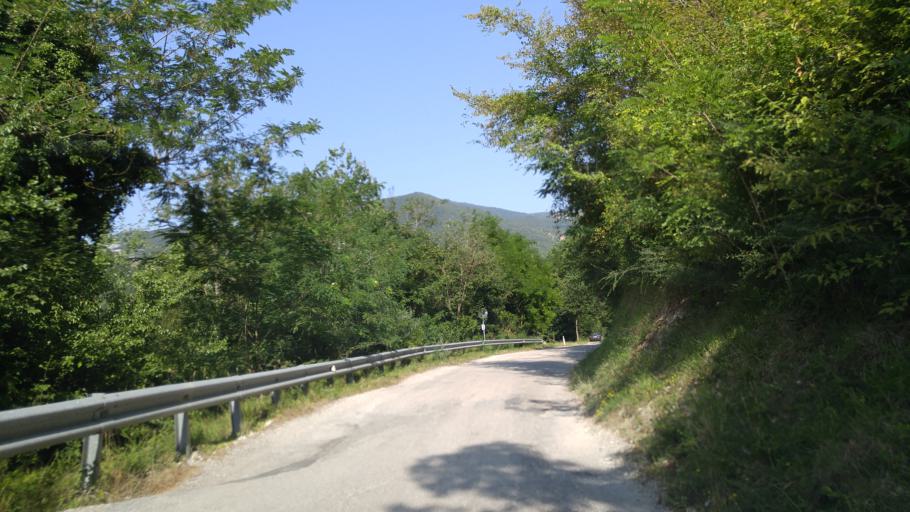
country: IT
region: The Marches
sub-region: Provincia di Pesaro e Urbino
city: Acqualagna
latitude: 43.6340
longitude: 12.6991
